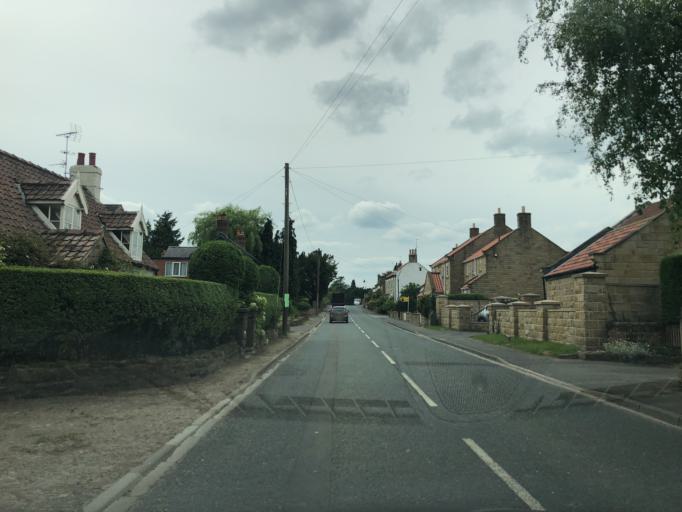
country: GB
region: England
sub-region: North Yorkshire
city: Angram Grange
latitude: 54.2361
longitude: -1.2555
